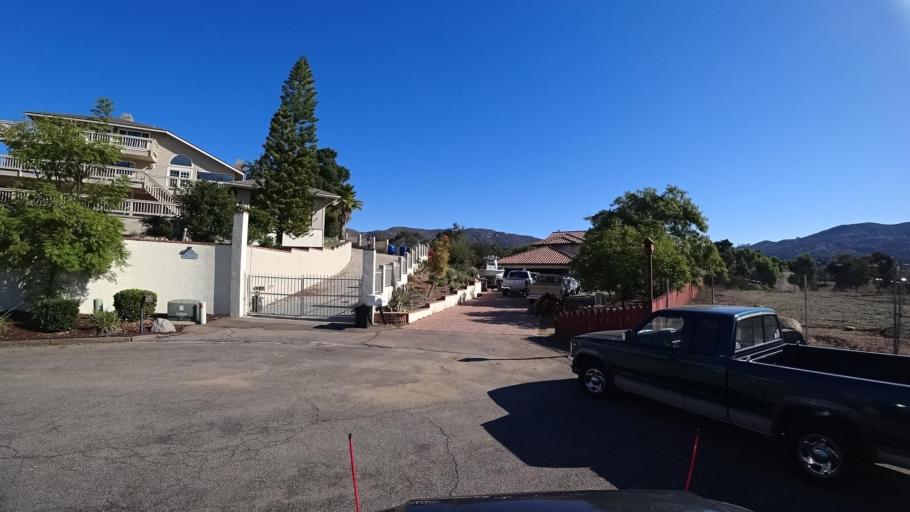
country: US
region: California
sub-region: San Diego County
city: Jamul
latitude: 32.7241
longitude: -116.8579
